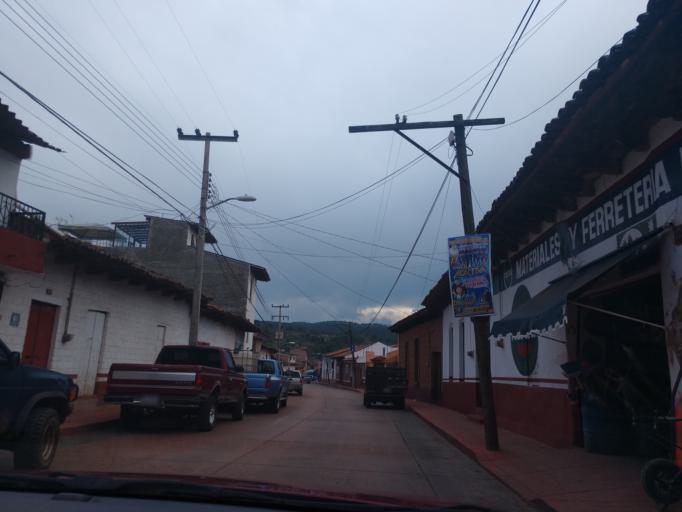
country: MX
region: Jalisco
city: La Manzanilla de la Paz
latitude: 20.0072
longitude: -103.1547
